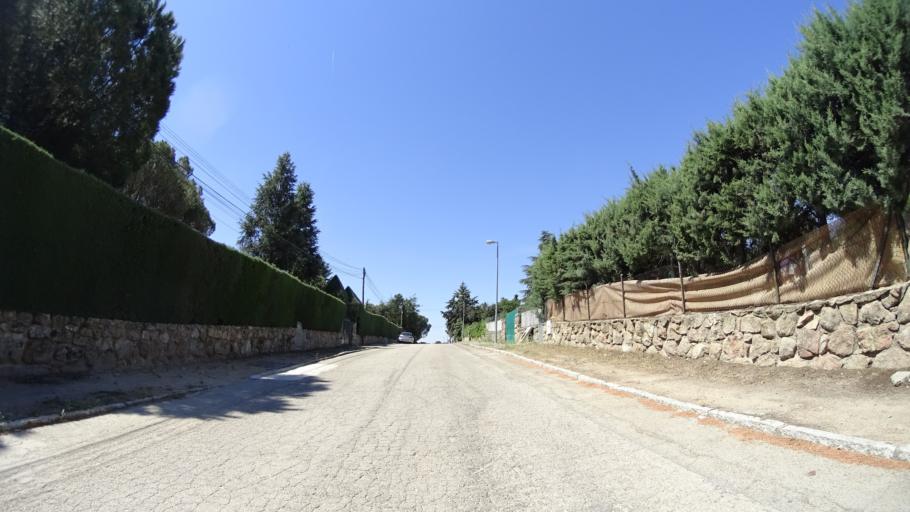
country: ES
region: Madrid
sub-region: Provincia de Madrid
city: Colmenarejo
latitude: 40.5483
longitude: -4.0042
